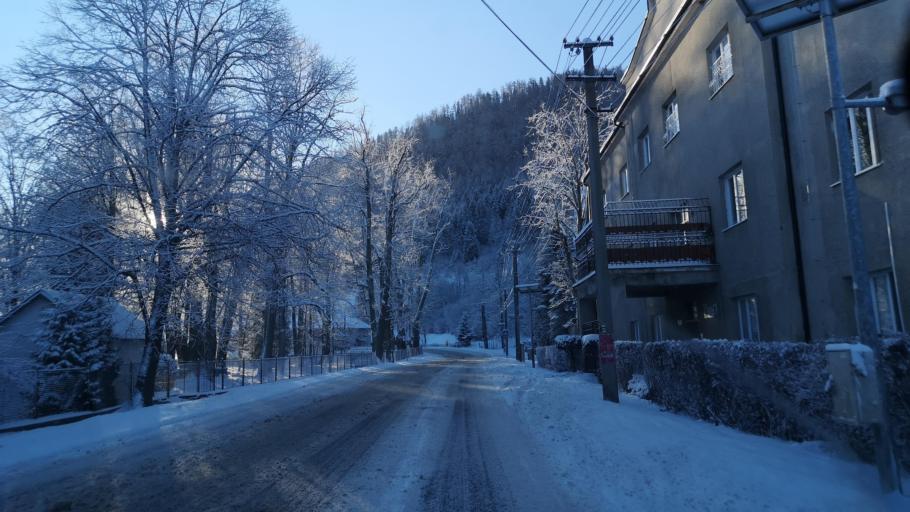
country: SK
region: Banskobystricky
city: Revuca
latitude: 48.8444
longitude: 20.0349
